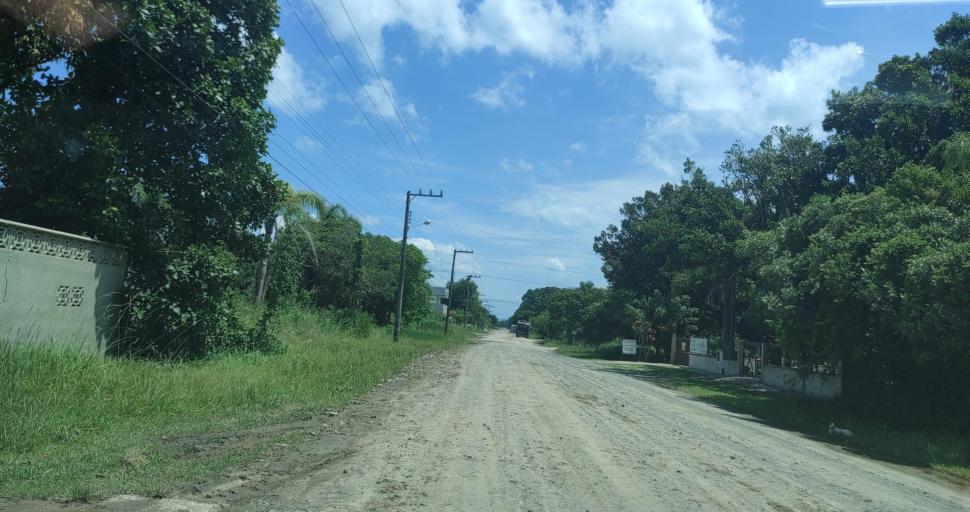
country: BR
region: Santa Catarina
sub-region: Porto Belo
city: Porto Belo
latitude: -27.1728
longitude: -48.5041
